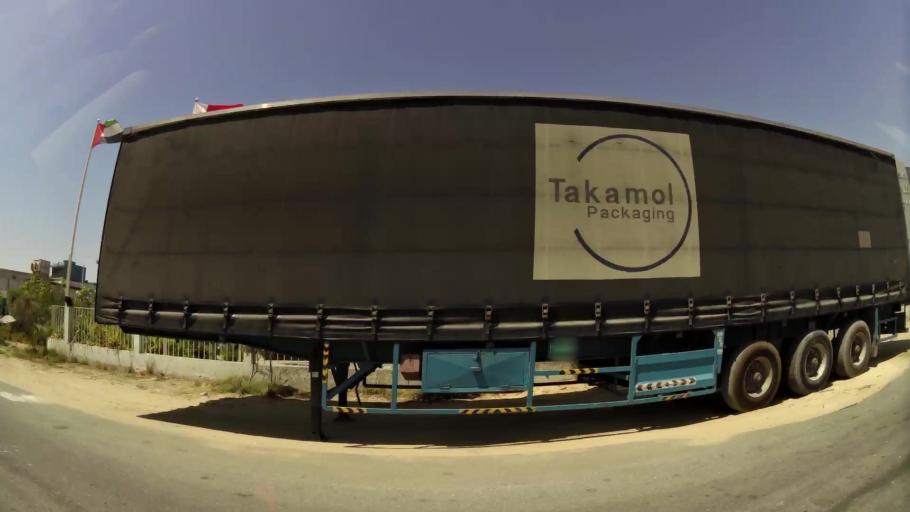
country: AE
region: Dubai
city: Dubai
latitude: 24.9810
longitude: 55.1638
